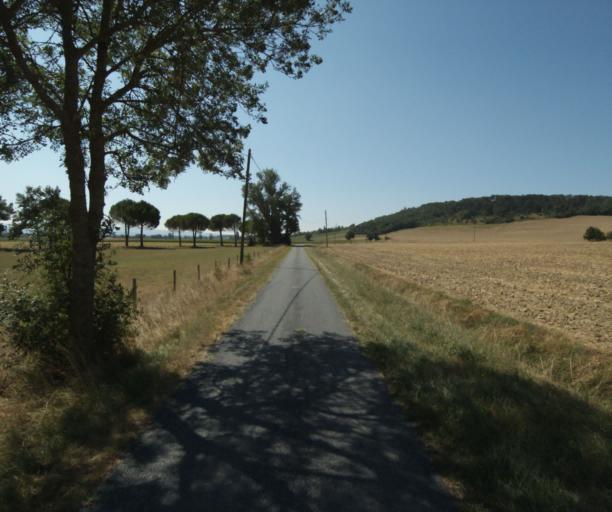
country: FR
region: Midi-Pyrenees
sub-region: Departement de la Haute-Garonne
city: Revel
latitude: 43.5188
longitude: 1.9496
